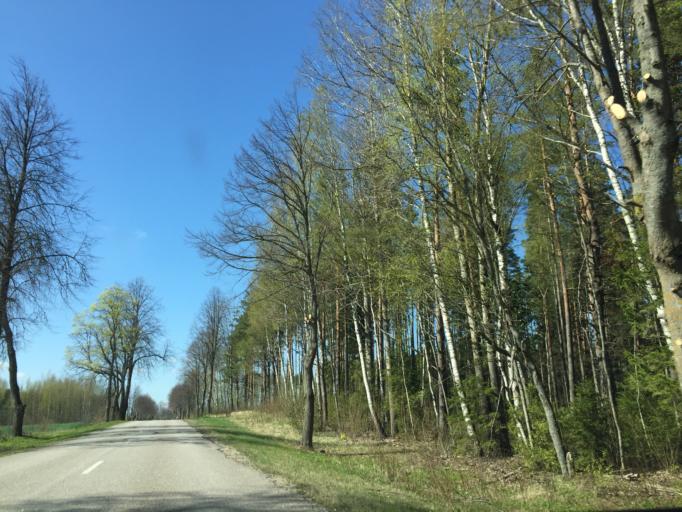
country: LV
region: Strenci
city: Seda
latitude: 57.5732
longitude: 25.7942
